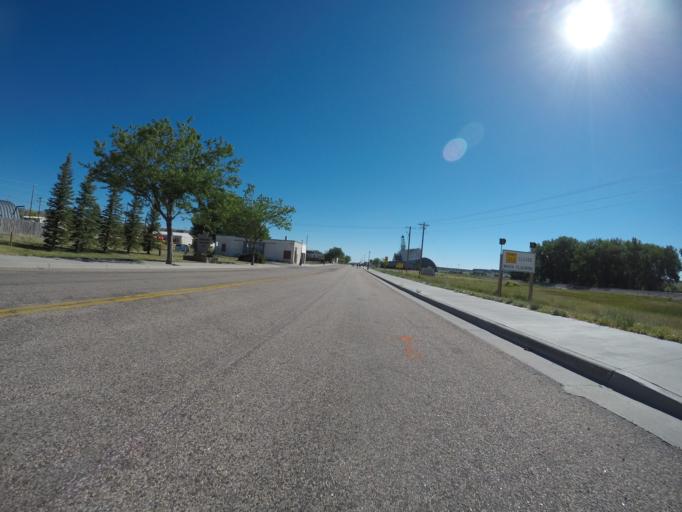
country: US
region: Wyoming
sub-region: Platte County
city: Wheatland
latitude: 41.7549
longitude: -104.8242
